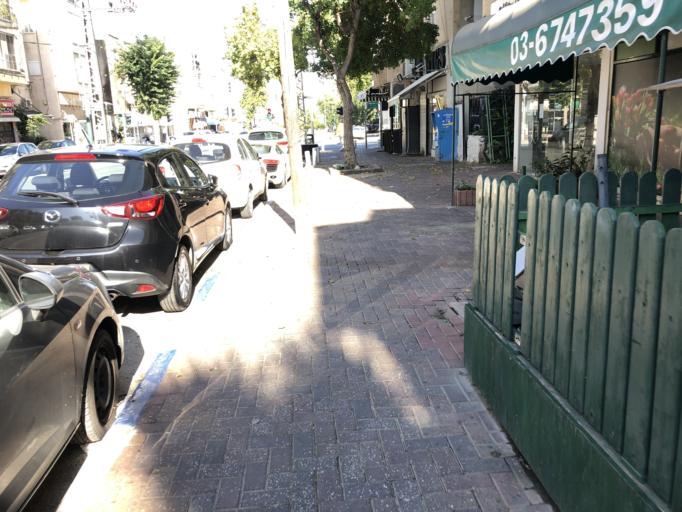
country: IL
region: Tel Aviv
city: Bene Beraq
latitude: 32.0779
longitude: 34.8252
